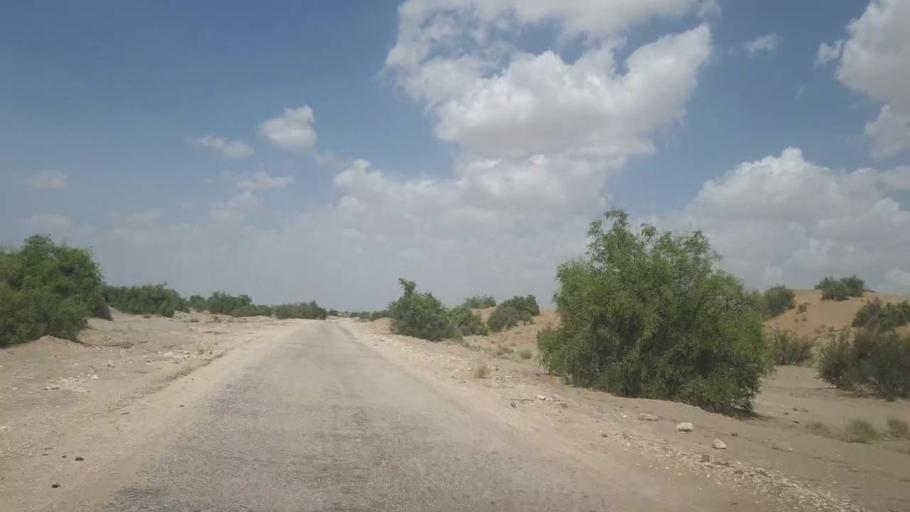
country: PK
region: Sindh
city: Kot Diji
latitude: 27.2542
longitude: 69.1653
